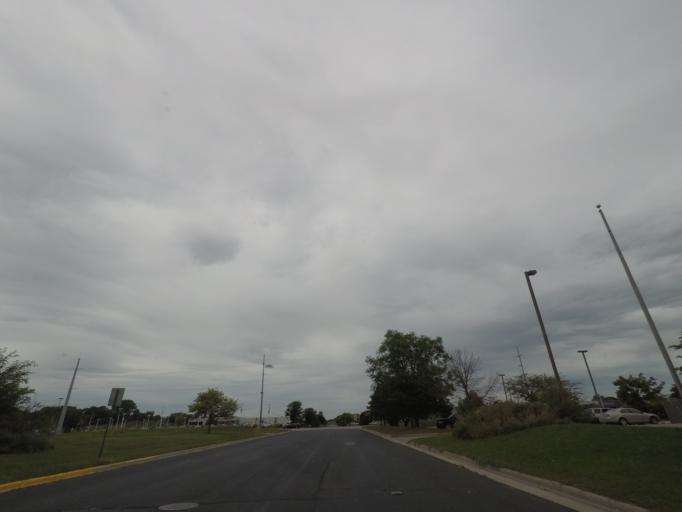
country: US
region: Wisconsin
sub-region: Dane County
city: Middleton
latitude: 43.1106
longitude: -89.5144
